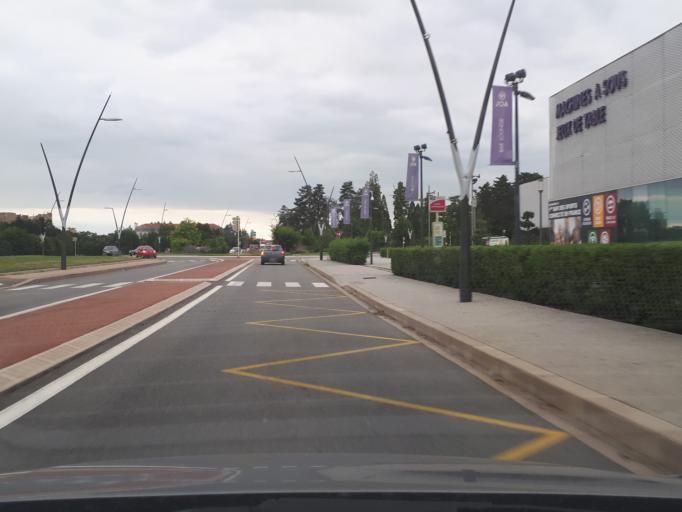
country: FR
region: Rhone-Alpes
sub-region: Departement de la Loire
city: Montrond-les-Bains
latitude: 45.6375
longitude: 4.2369
